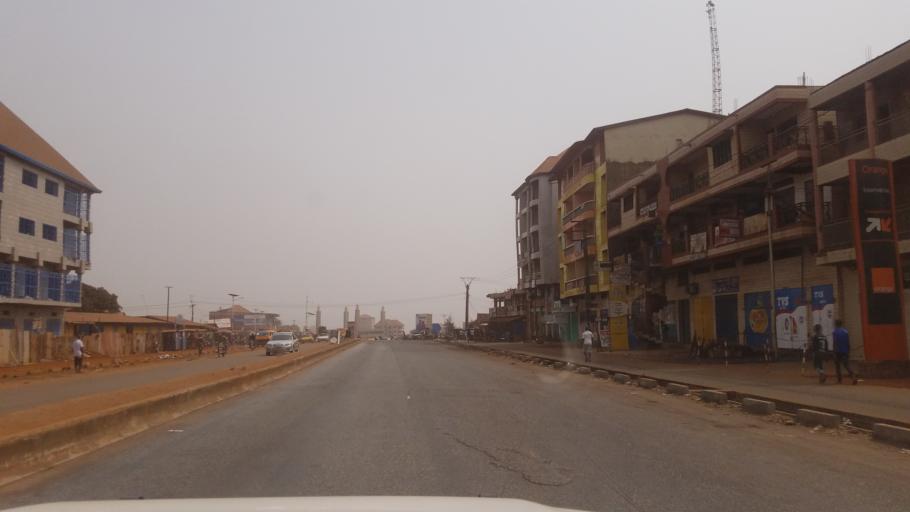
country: GN
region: Kindia
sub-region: Prefecture de Dubreka
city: Dubreka
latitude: 9.6808
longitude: -13.5355
